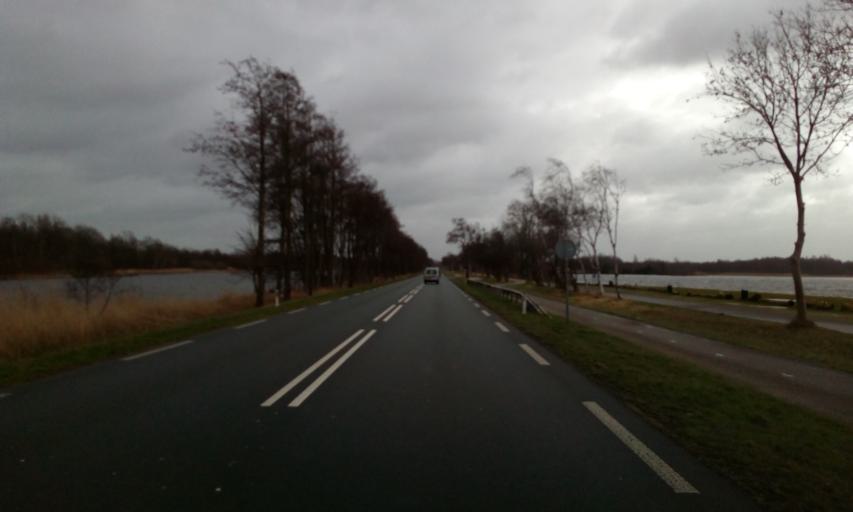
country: NL
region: North Holland
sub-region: Gemeente Wijdemeren
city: Oud-Loosdrecht
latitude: 52.2319
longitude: 5.0693
